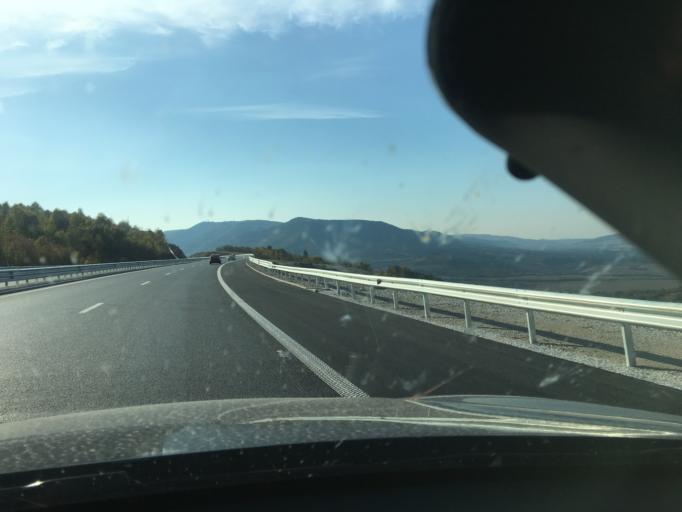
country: BG
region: Lovech
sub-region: Obshtina Yablanitsa
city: Yablanitsa
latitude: 43.0479
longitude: 24.1381
